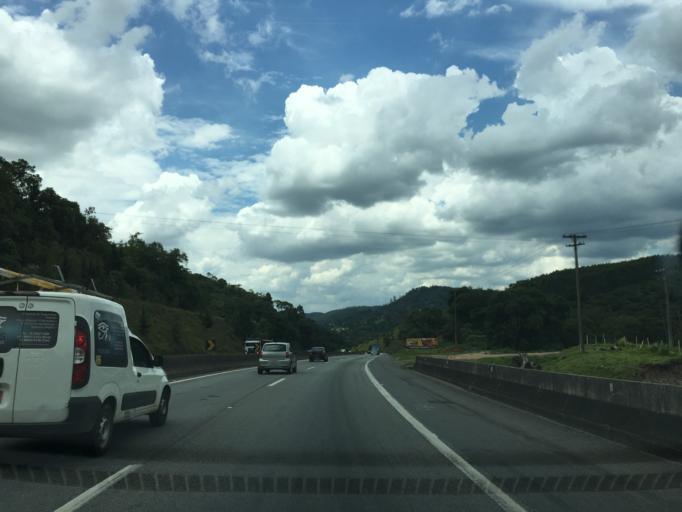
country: BR
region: Sao Paulo
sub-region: Mairipora
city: Mairipora
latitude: -23.2323
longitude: -46.6015
